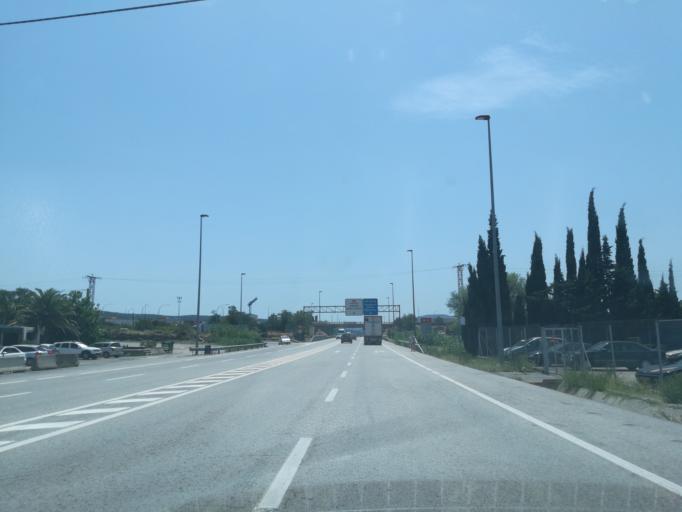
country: ES
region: Catalonia
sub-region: Provincia de Girona
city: la Jonquera
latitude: 42.4094
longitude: 2.8770
